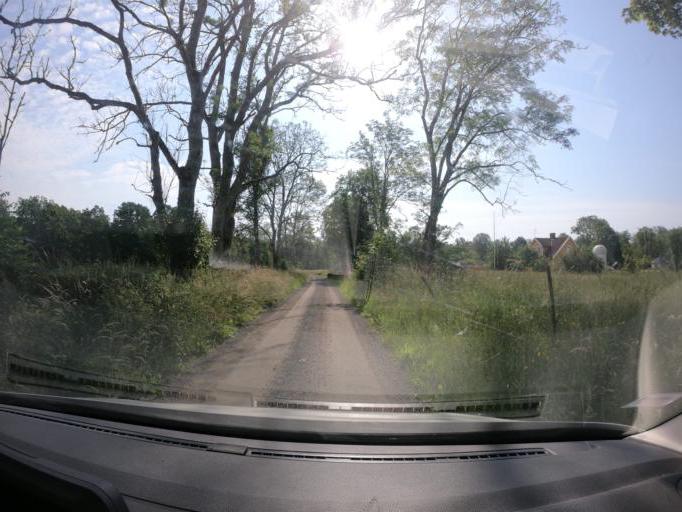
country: SE
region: Skane
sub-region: Hassleholms Kommun
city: Bjarnum
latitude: 56.2176
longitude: 13.5667
